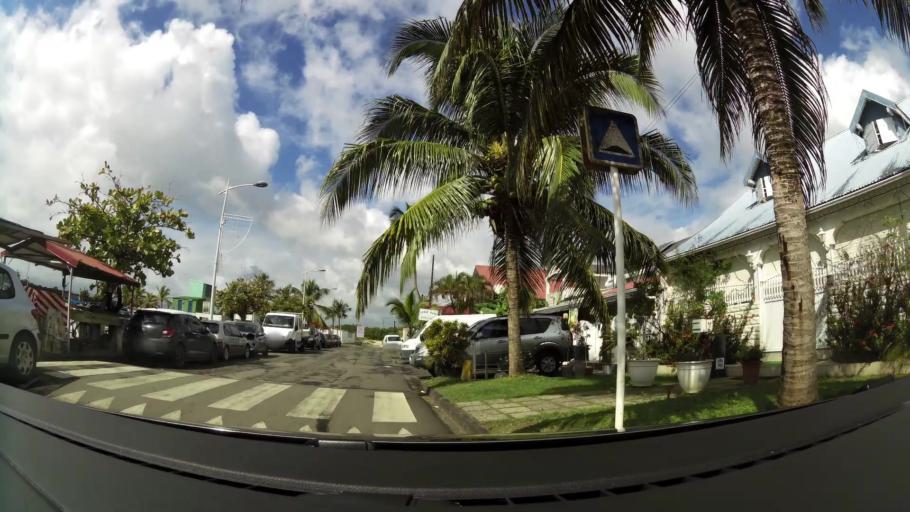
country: GP
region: Guadeloupe
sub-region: Guadeloupe
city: Pointe-a-Pitre
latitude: 16.2511
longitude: -61.5477
